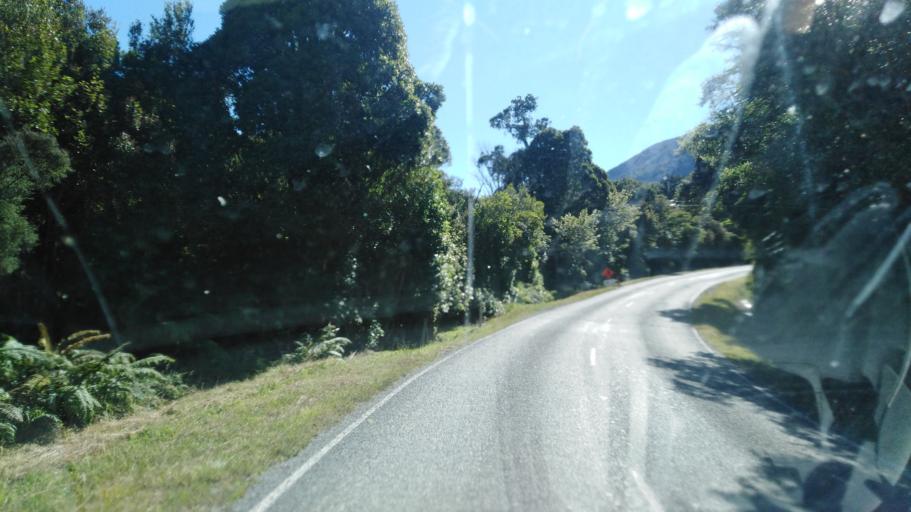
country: NZ
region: West Coast
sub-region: Buller District
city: Westport
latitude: -41.5278
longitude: 171.9976
